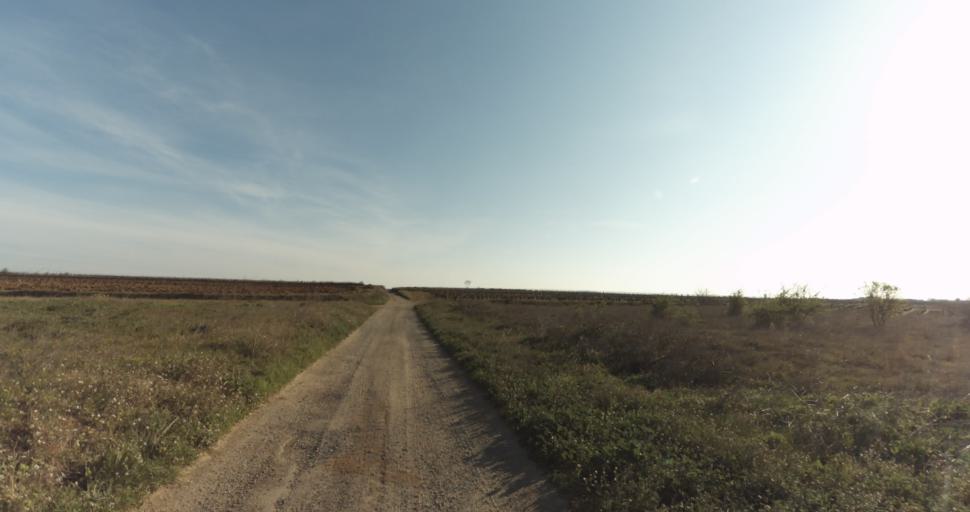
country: FR
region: Languedoc-Roussillon
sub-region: Departement de l'Herault
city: Marseillan
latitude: 43.3557
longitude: 3.5013
